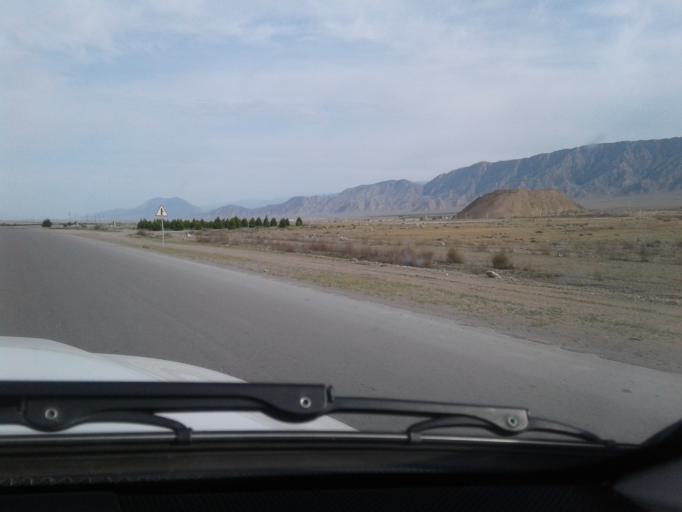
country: TM
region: Ahal
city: Arcabil
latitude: 38.2193
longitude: 57.8025
